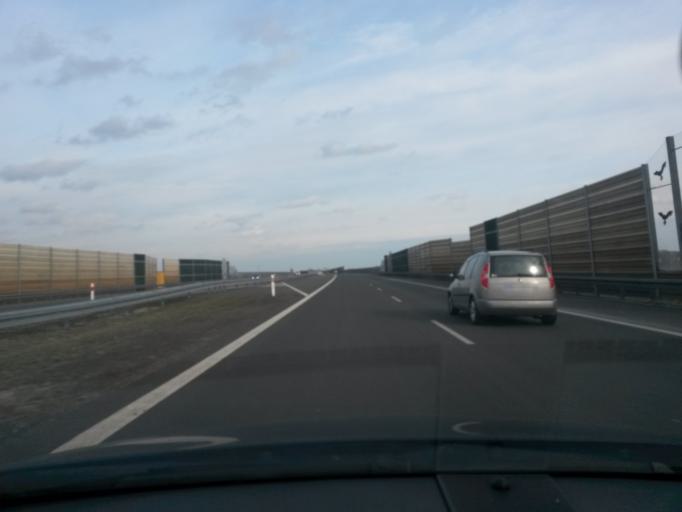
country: PL
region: Greater Poland Voivodeship
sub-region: Powiat turecki
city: Brudzew
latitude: 52.1228
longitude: 18.6846
